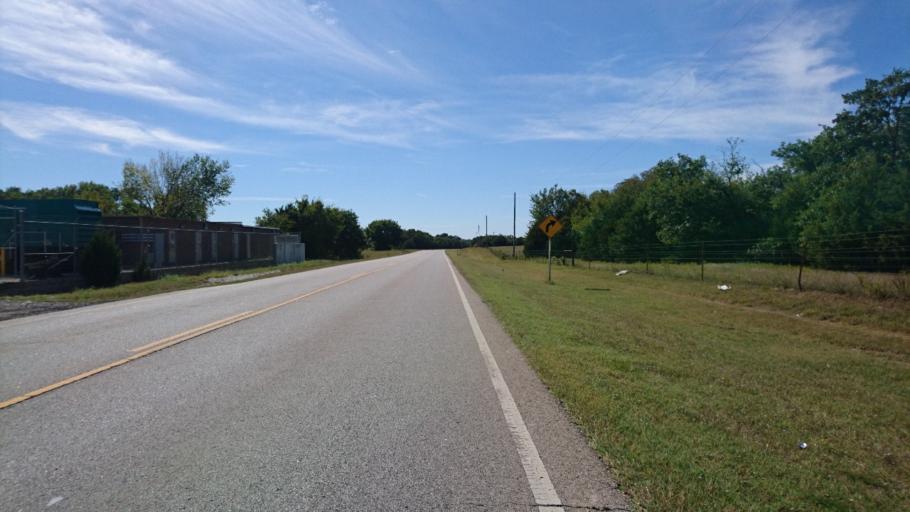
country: US
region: Oklahoma
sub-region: Lincoln County
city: Stroud
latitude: 35.7413
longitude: -96.7067
